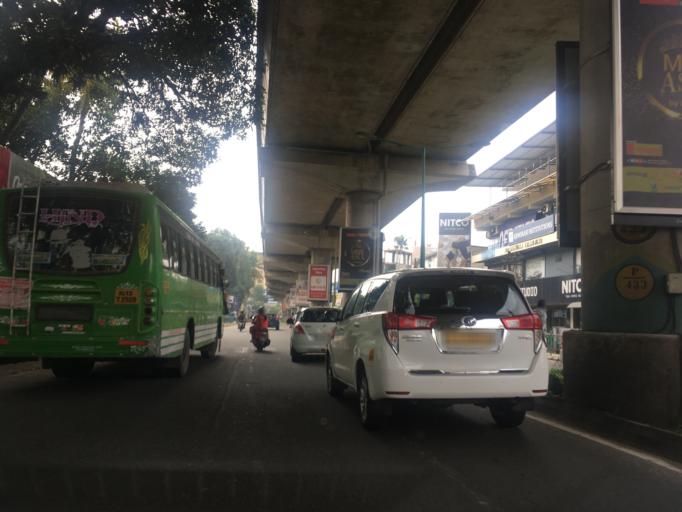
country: IN
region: Kerala
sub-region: Ernakulam
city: Elur
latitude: 10.0208
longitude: 76.3057
